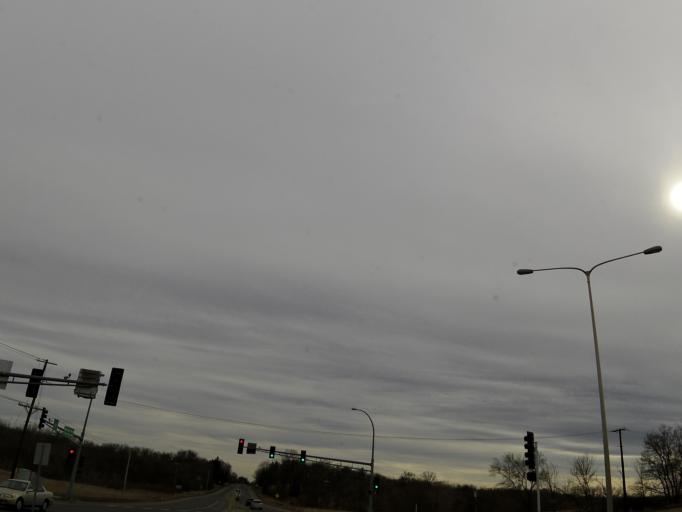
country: US
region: Minnesota
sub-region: Scott County
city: Prior Lake
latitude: 44.7179
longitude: -93.3791
